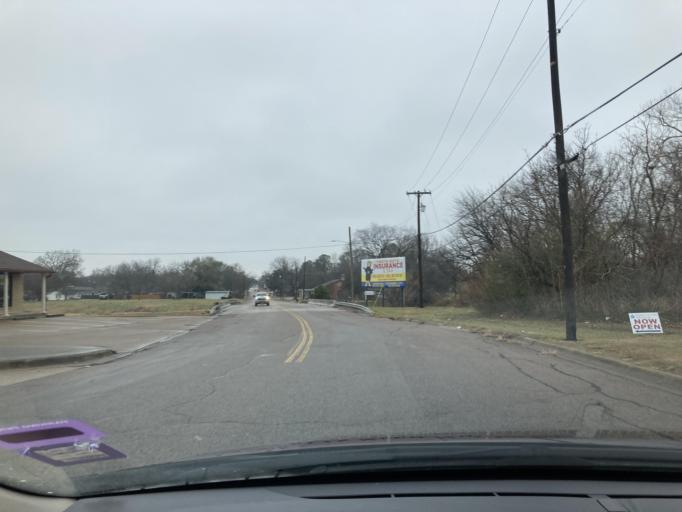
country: US
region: Texas
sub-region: Navarro County
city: Corsicana
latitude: 32.1003
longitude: -96.4681
